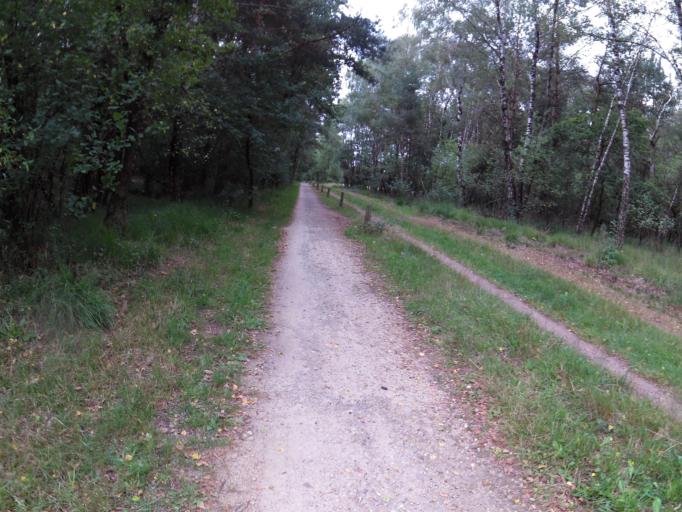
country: DE
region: Lower Saxony
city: Bad Bentheim
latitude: 52.2511
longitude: 7.1036
